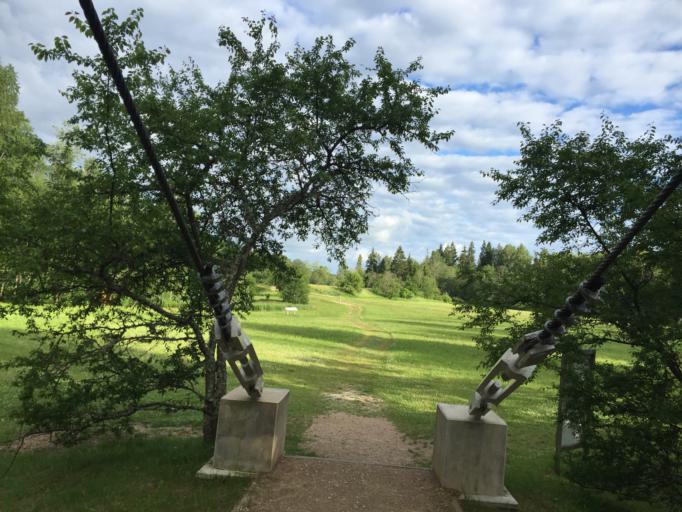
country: LV
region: Ligatne
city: Ligatne
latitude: 57.2472
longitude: 25.1437
